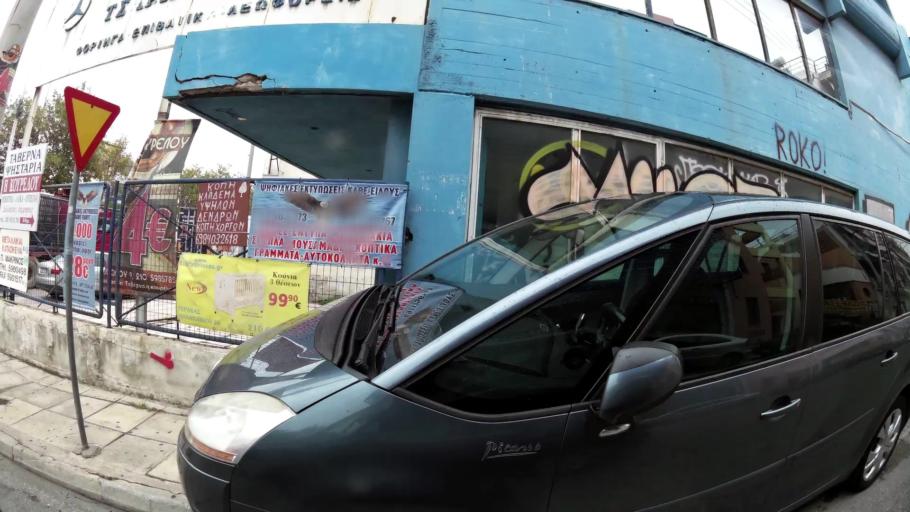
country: GR
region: Attica
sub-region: Nomarchia Athinas
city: Peristeri
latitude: 37.9989
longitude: 23.6898
